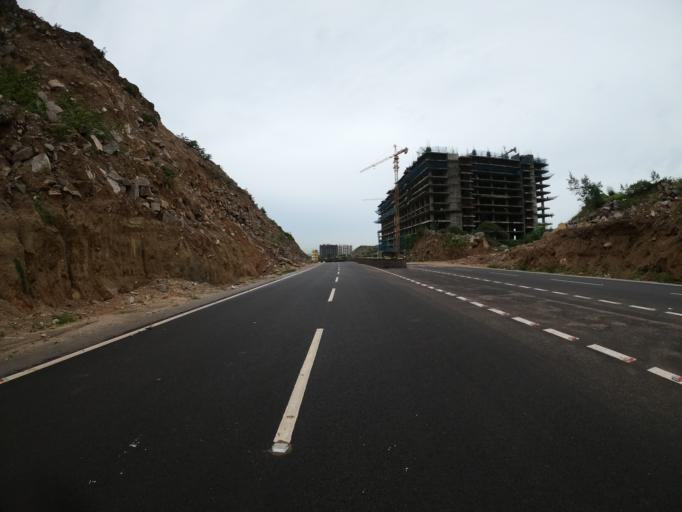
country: IN
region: Telangana
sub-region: Rangareddi
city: Kukatpalli
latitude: 17.4633
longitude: 78.3823
